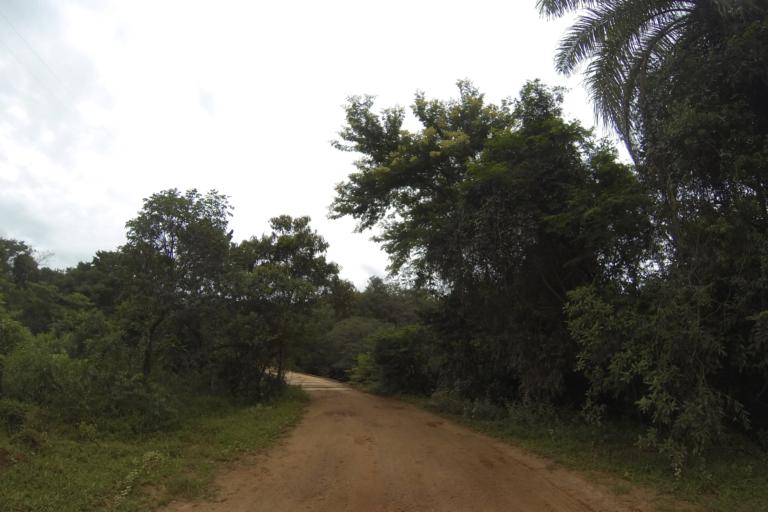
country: BR
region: Minas Gerais
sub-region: Ibia
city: Ibia
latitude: -19.7401
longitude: -46.5469
